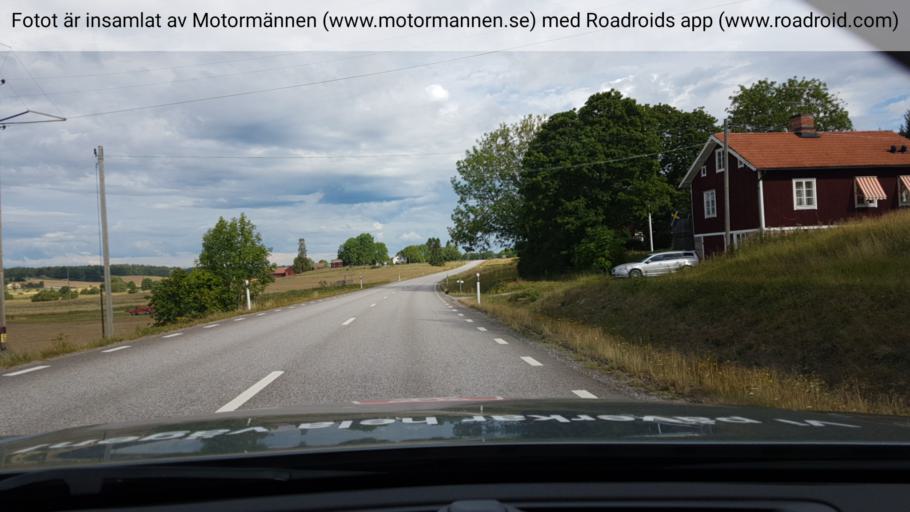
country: SE
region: Uppsala
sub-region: Heby Kommun
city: Morgongava
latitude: 59.8897
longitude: 16.9069
